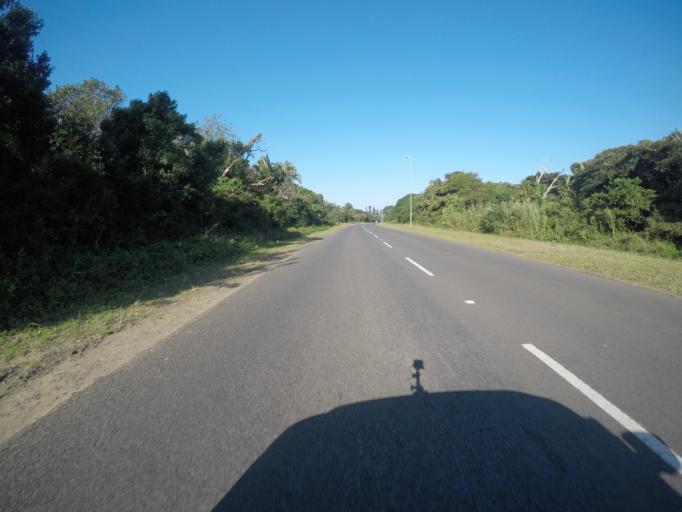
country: ZA
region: KwaZulu-Natal
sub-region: uThungulu District Municipality
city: Richards Bay
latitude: -28.7877
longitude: 32.0864
